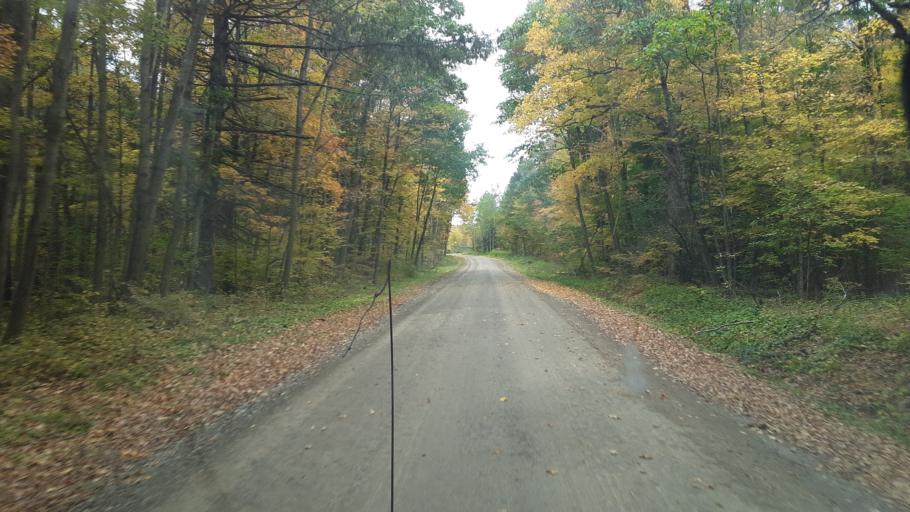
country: US
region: New York
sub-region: Allegany County
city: Alfred
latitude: 42.3744
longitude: -77.8499
